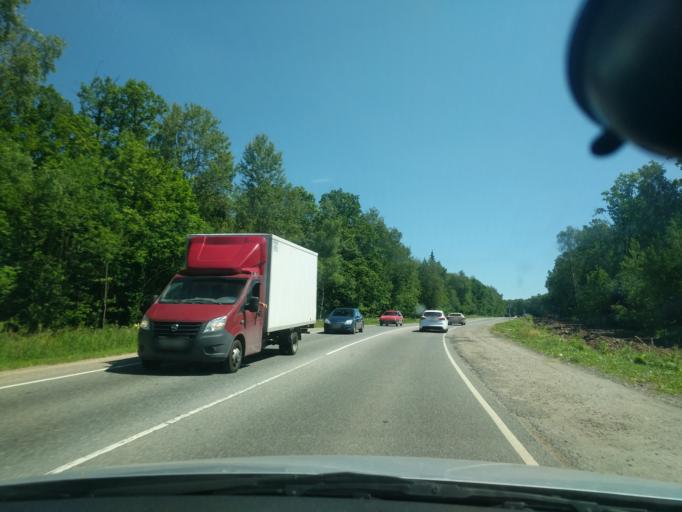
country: RU
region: Moskovskaya
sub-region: Chekhovskiy Rayon
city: Chekhov
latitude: 55.1440
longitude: 37.5028
